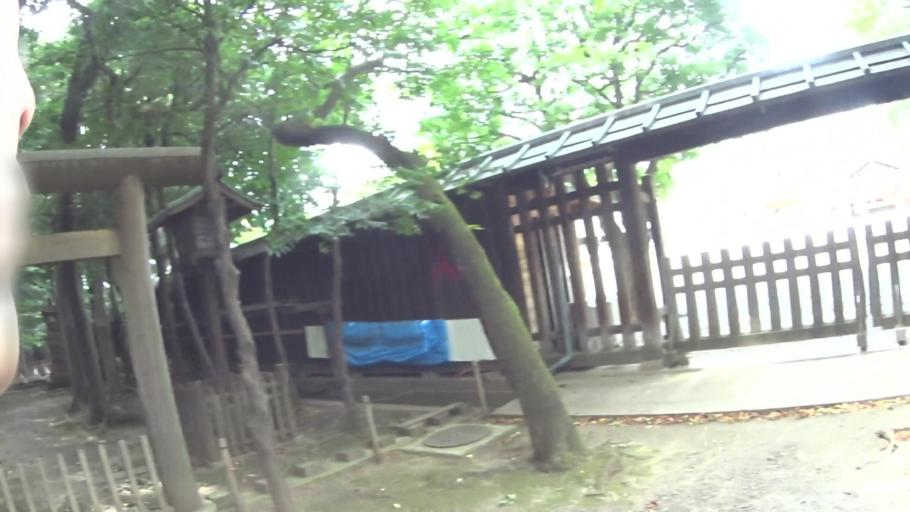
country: JP
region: Tokyo
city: Tokyo
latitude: 35.6937
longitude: 139.7436
